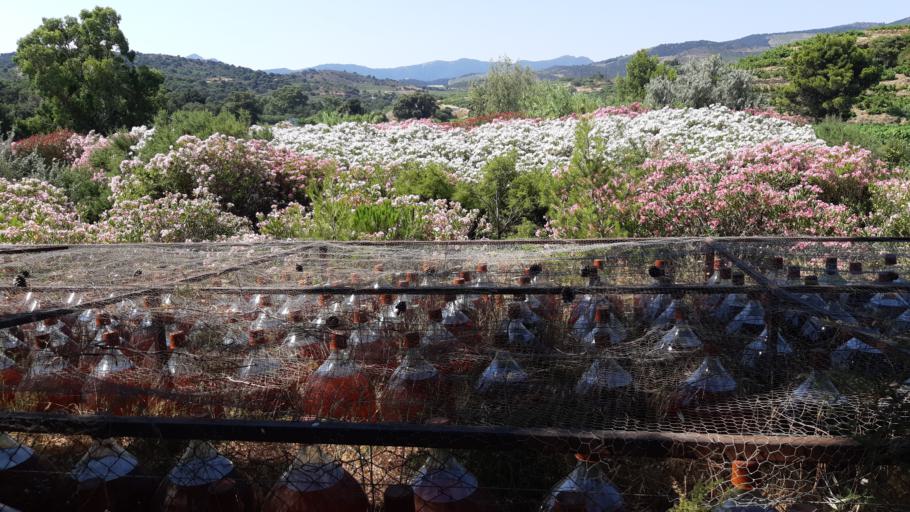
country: FR
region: Languedoc-Roussillon
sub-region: Departement des Pyrenees-Orientales
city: Portvendres
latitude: 42.5060
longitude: 3.1216
